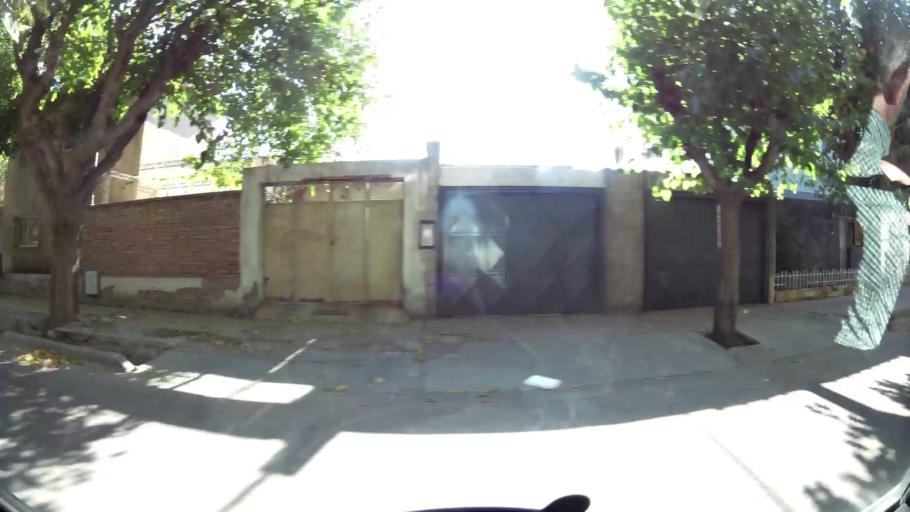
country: AR
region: Mendoza
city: Mendoza
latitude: -32.9111
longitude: -68.8244
